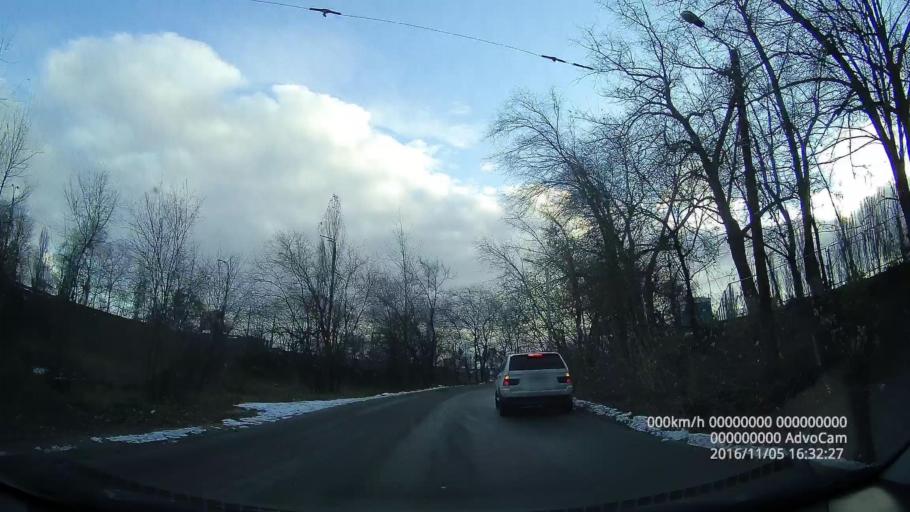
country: RU
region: Voronezj
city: Voronezh
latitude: 51.6852
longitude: 39.2167
